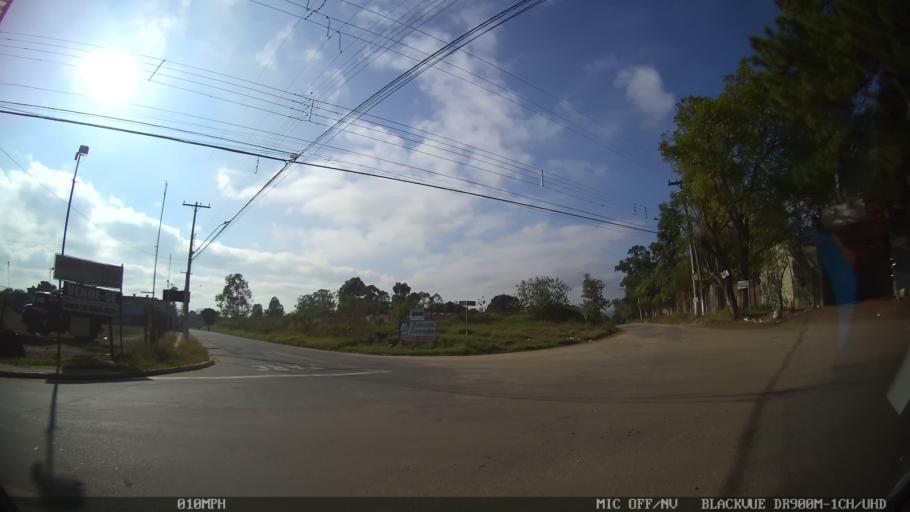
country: BR
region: Sao Paulo
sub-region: Hortolandia
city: Hortolandia
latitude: -22.9060
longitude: -47.1714
